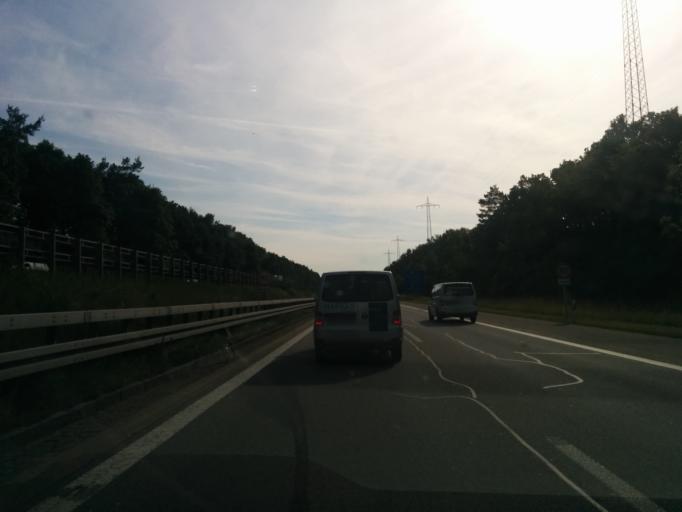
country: DE
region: Bavaria
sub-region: Upper Bavaria
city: Germering
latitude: 48.1134
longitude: 11.3595
